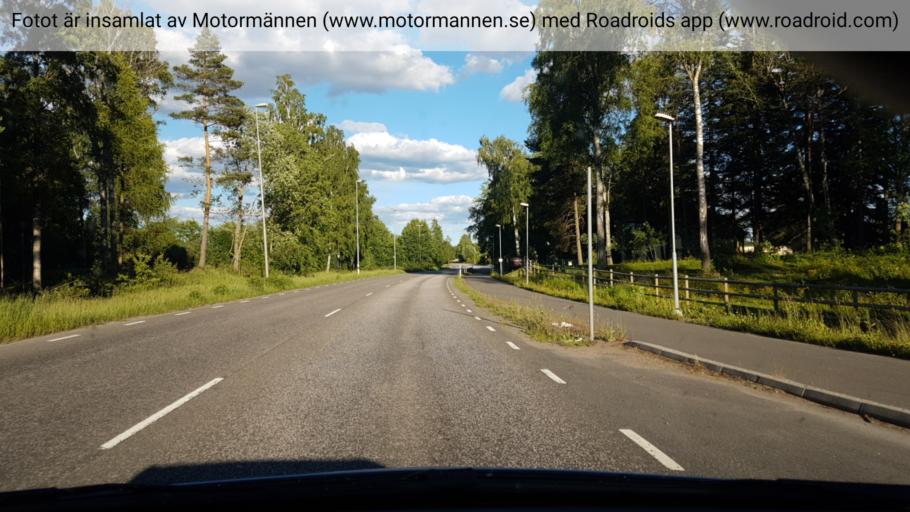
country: SE
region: Vaestra Goetaland
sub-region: Tidaholms Kommun
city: Tidaholm
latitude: 58.1915
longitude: 13.9406
